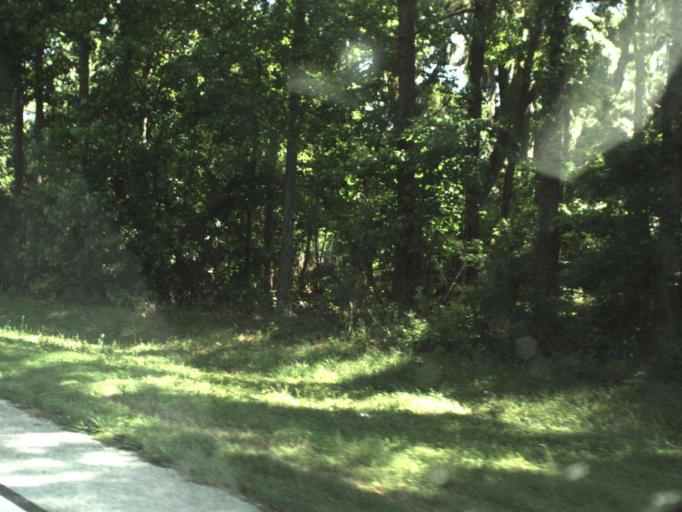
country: US
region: Florida
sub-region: Marion County
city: Belleview
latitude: 29.1014
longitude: -82.0902
